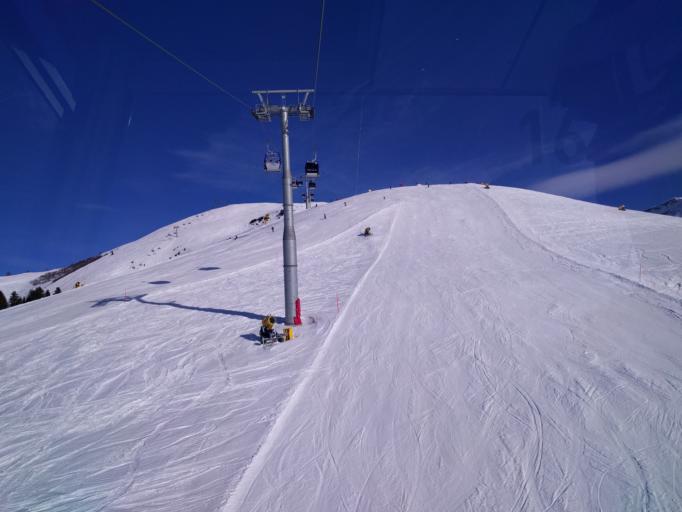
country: CH
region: Bern
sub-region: Obersimmental-Saanen District
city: Lenk
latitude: 46.4442
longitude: 7.4789
